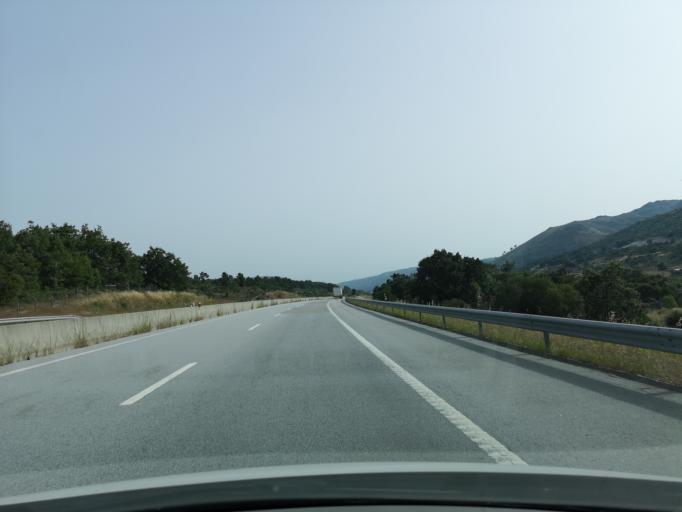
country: PT
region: Castelo Branco
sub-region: Belmonte
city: Belmonte
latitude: 40.4171
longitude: -7.2866
